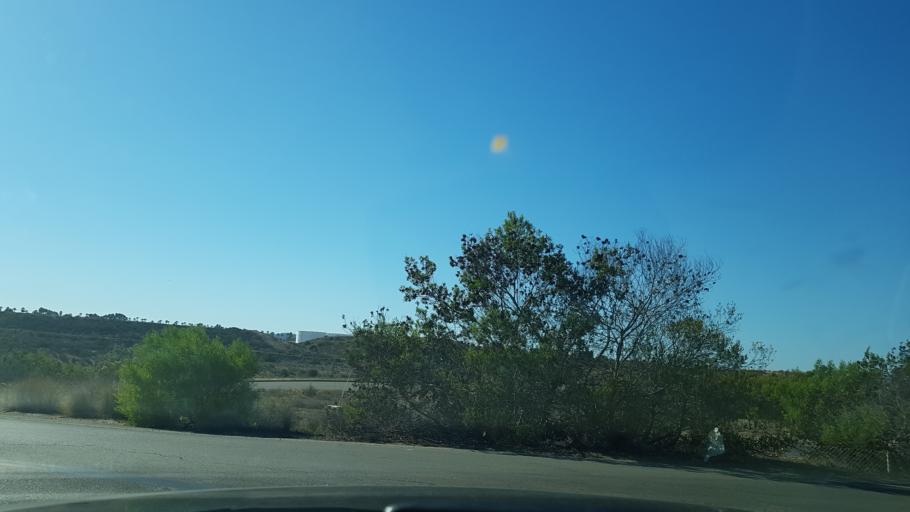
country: US
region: California
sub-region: San Diego County
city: La Jolla
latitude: 32.8400
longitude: -117.1513
